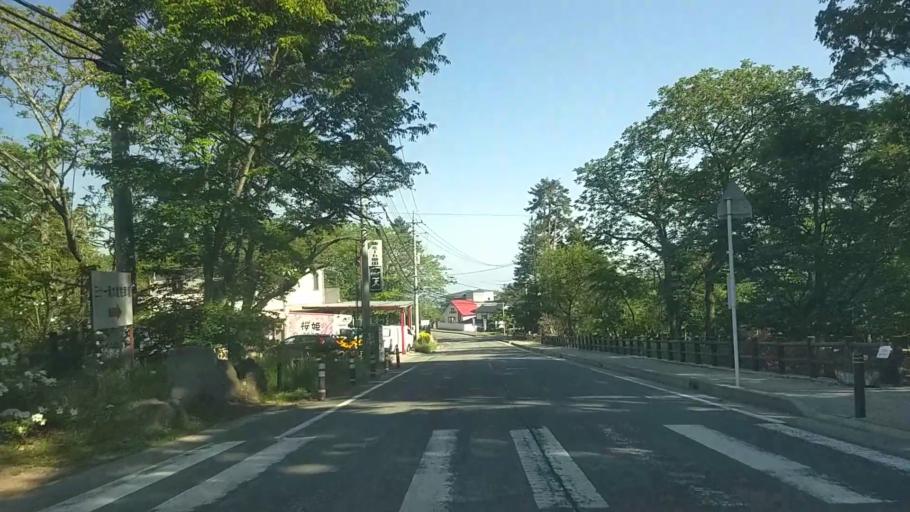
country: JP
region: Yamanashi
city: Nirasaki
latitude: 35.8779
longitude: 138.3553
